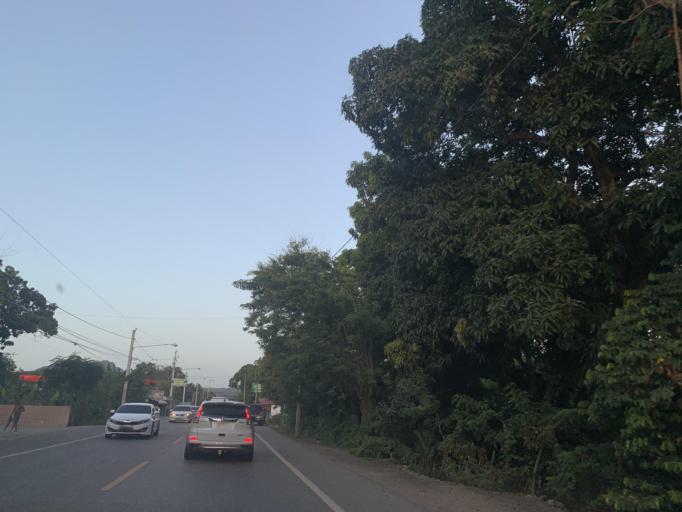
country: DO
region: Puerto Plata
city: Imbert
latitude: 19.7931
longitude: -70.8056
